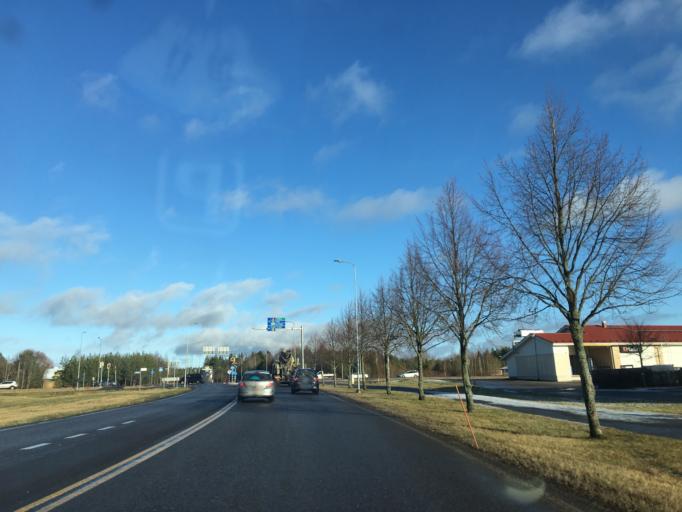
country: FI
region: Varsinais-Suomi
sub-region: Turku
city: Raisio
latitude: 60.5016
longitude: 22.1488
